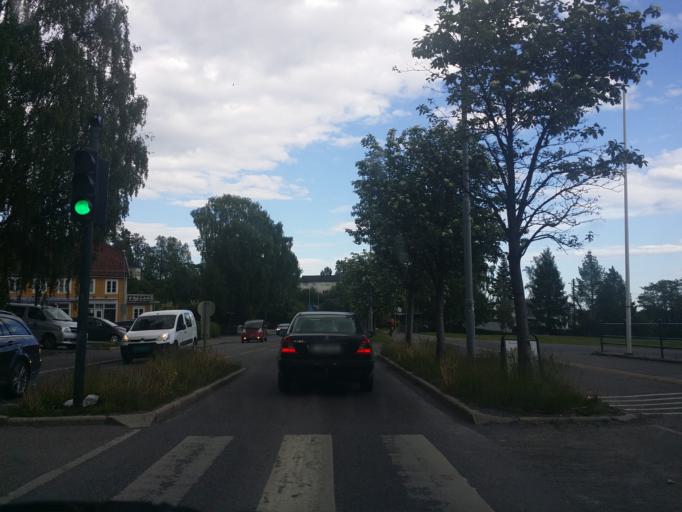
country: NO
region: Oslo
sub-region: Oslo
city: Sjolyststranda
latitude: 59.9418
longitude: 10.6720
